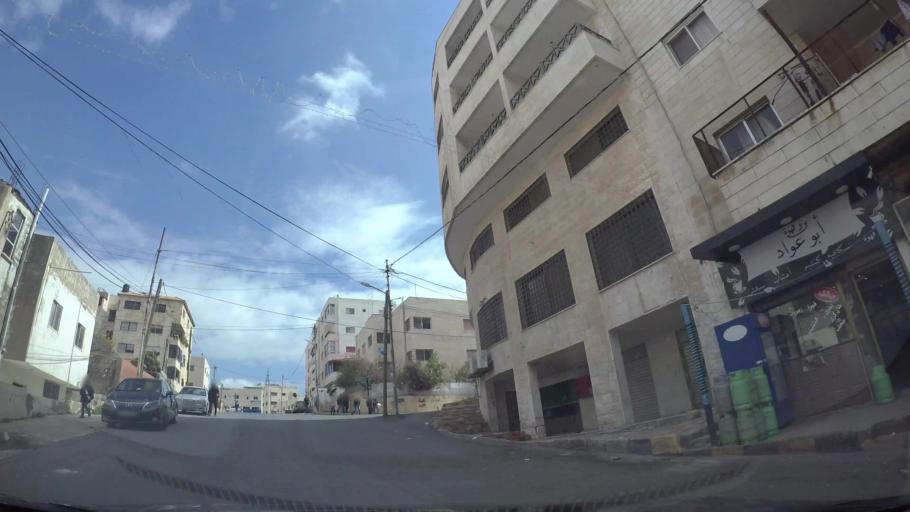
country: JO
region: Amman
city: Wadi as Sir
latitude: 31.9593
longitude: 35.8361
